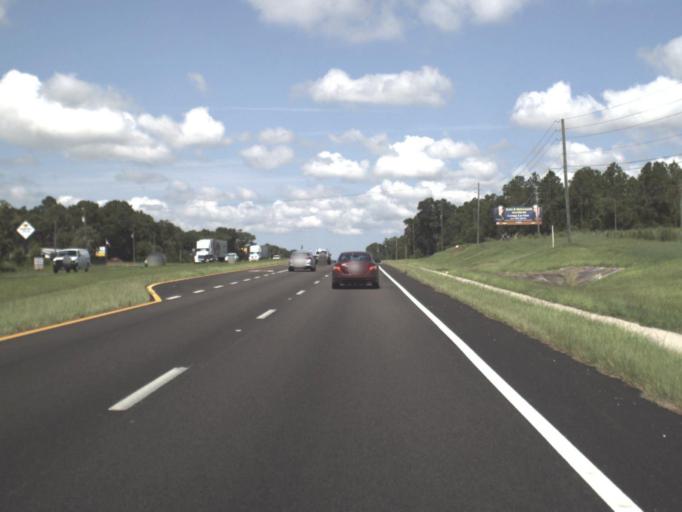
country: US
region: Florida
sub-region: Hernando County
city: Brookridge
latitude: 28.5413
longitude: -82.4481
